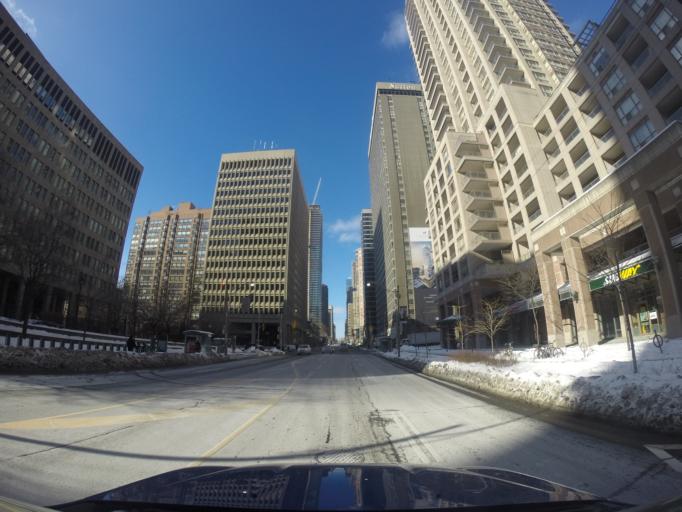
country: CA
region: Ontario
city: Toronto
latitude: 43.6637
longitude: -79.3868
